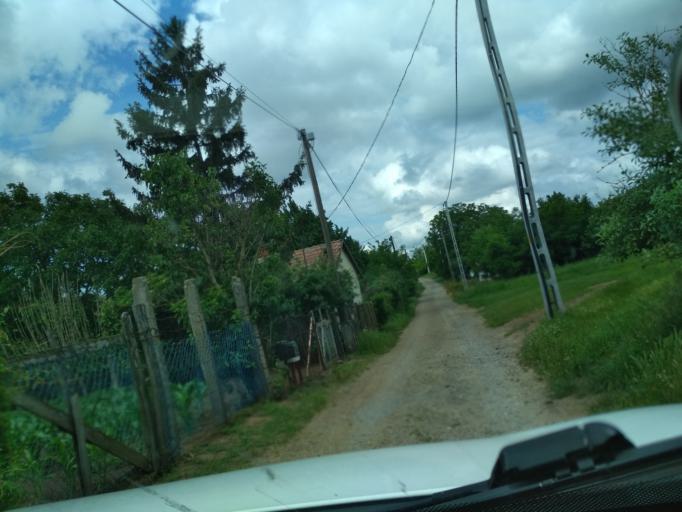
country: HU
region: Jasz-Nagykun-Szolnok
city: Tiszafured
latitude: 47.6089
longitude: 20.7445
